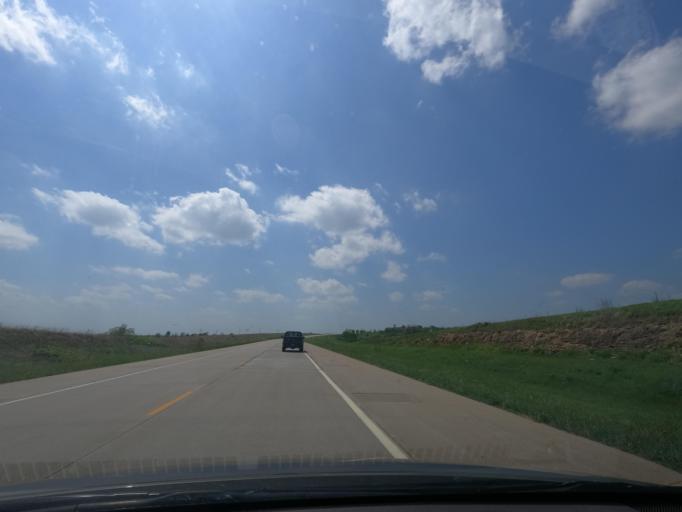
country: US
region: Kansas
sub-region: Elk County
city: Howard
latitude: 37.6281
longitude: -96.1340
